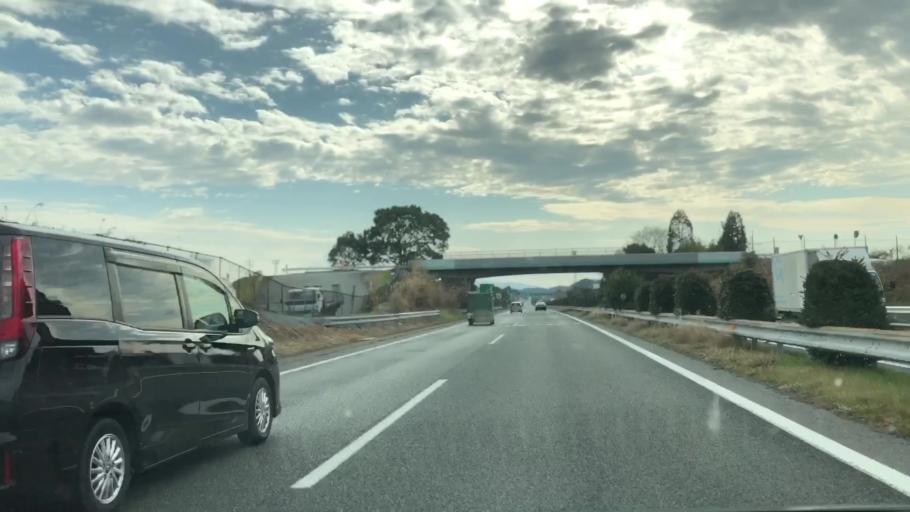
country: JP
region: Fukuoka
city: Kurume
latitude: 33.2653
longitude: 130.5389
